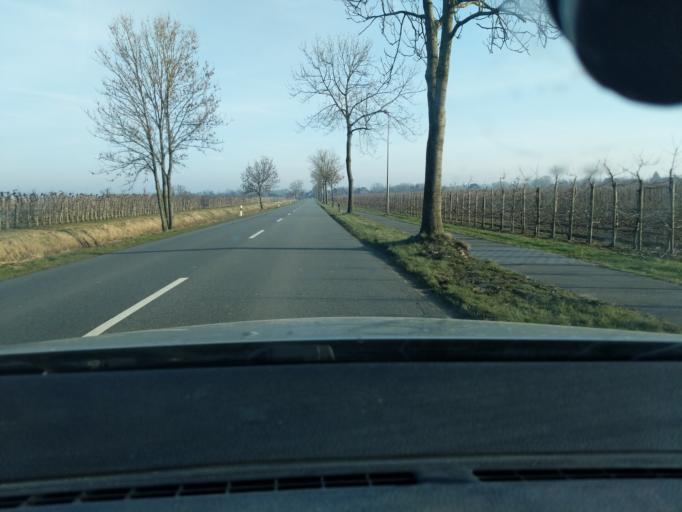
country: DE
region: Lower Saxony
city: Jork
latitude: 53.5444
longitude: 9.6602
